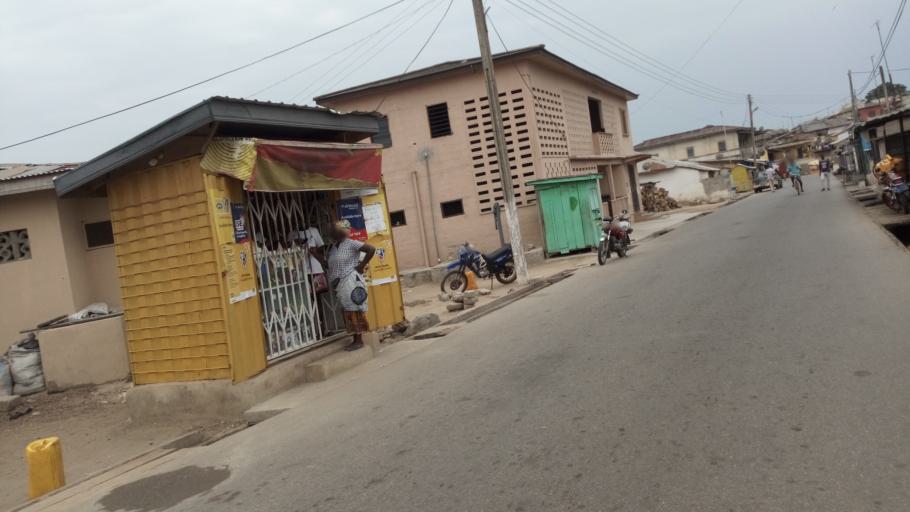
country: GH
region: Central
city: Winneba
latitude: 5.3409
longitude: -0.6219
